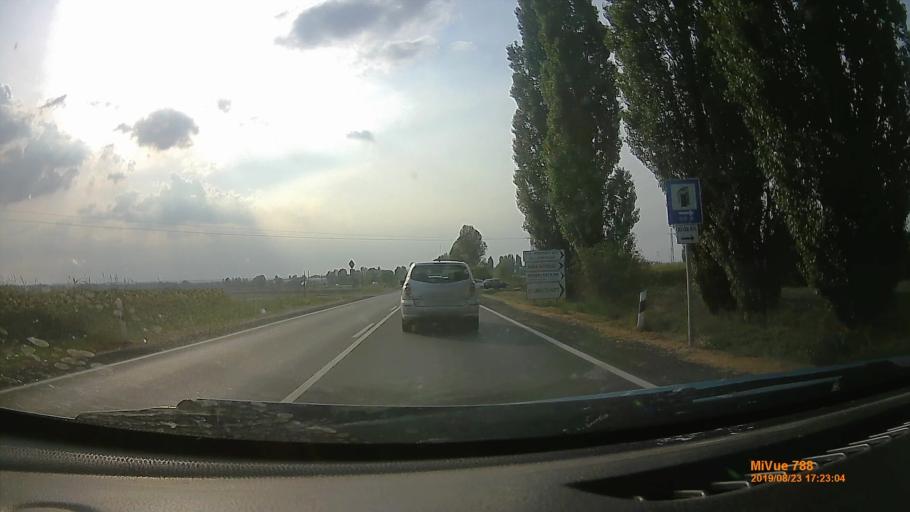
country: HU
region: Pest
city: Erd
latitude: 47.3625
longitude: 18.8934
